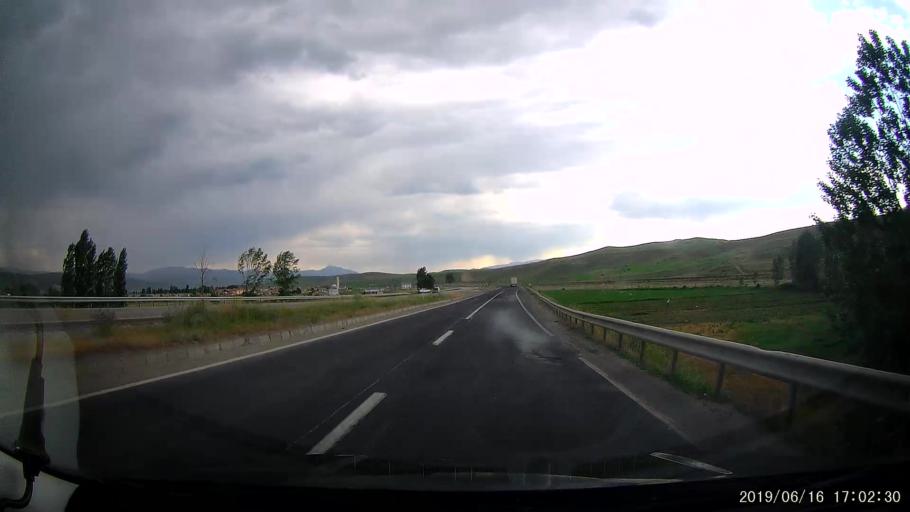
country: TR
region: Erzurum
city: Askale
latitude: 39.9402
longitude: 40.7530
